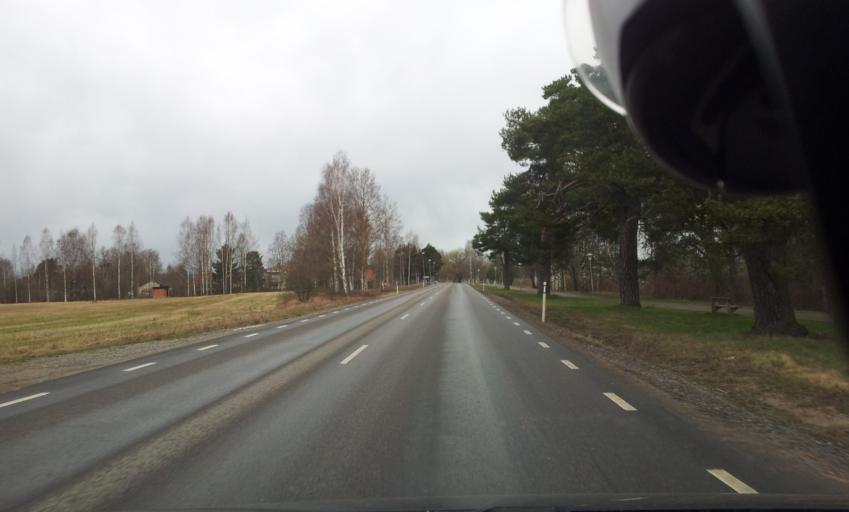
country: SE
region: Gaevleborg
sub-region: Ljusdals Kommun
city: Ljusdal
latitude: 61.8219
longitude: 16.0794
